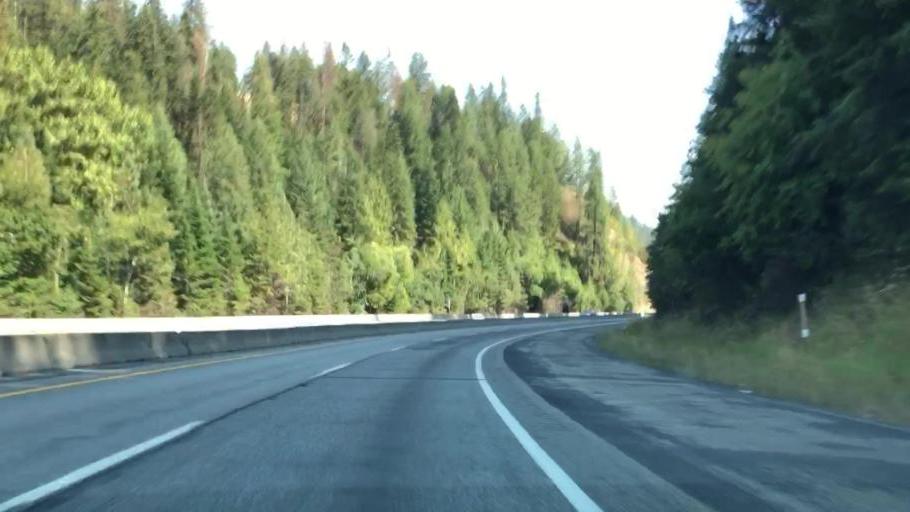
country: US
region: Idaho
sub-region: Shoshone County
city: Pinehurst
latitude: 47.5907
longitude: -116.4840
